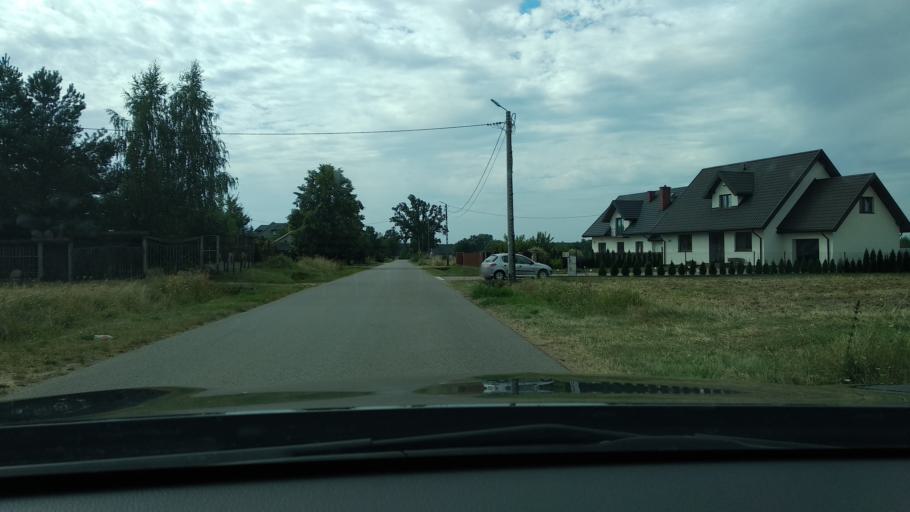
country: PL
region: Masovian Voivodeship
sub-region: Powiat pultuski
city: Zatory
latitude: 52.6533
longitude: 21.1865
